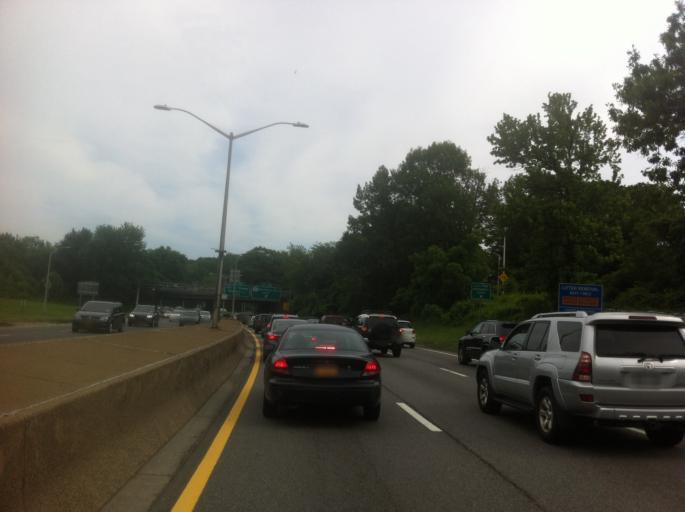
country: US
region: New York
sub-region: Nassau County
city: East Atlantic Beach
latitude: 40.7635
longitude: -73.7582
